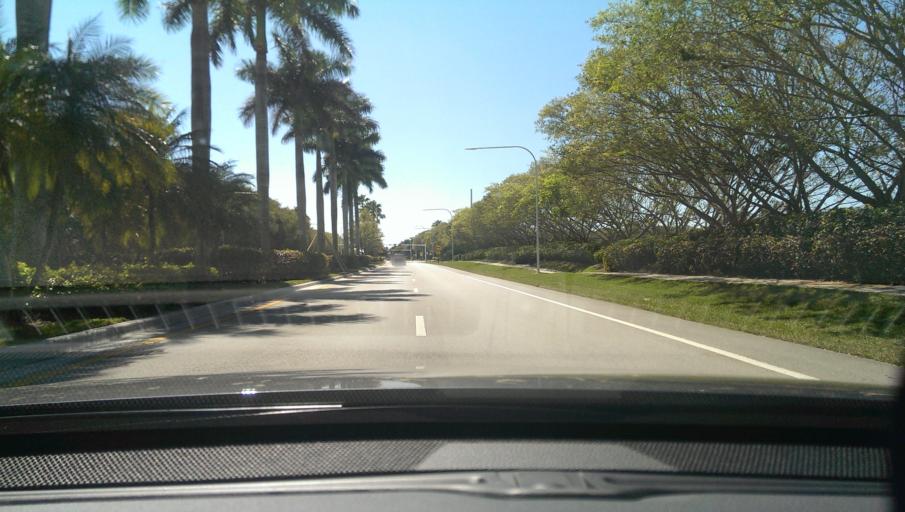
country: US
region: Florida
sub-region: Broward County
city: Weston
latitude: 26.0723
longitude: -80.3936
